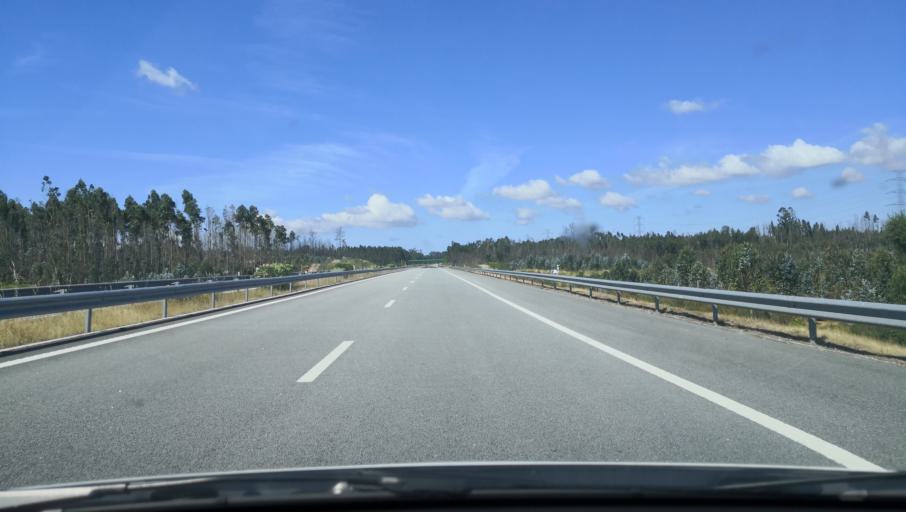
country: PT
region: Coimbra
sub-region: Cantanhede
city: Cantanhede
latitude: 40.2834
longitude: -8.5791
